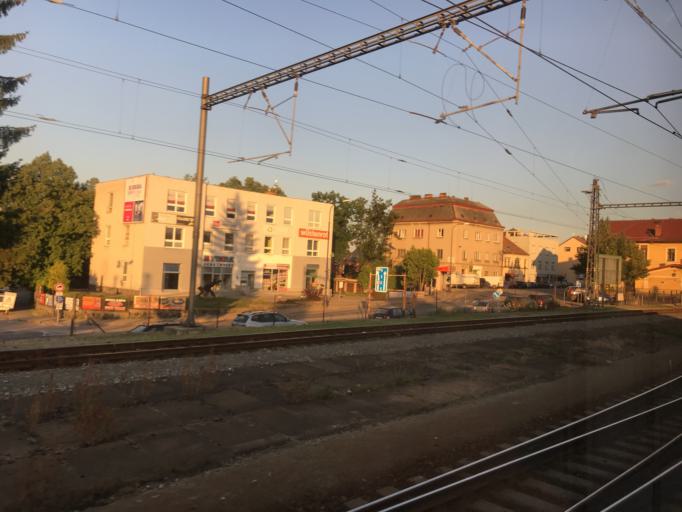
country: CZ
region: Central Bohemia
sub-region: Okres Benesov
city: Benesov
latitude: 49.7812
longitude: 14.6818
